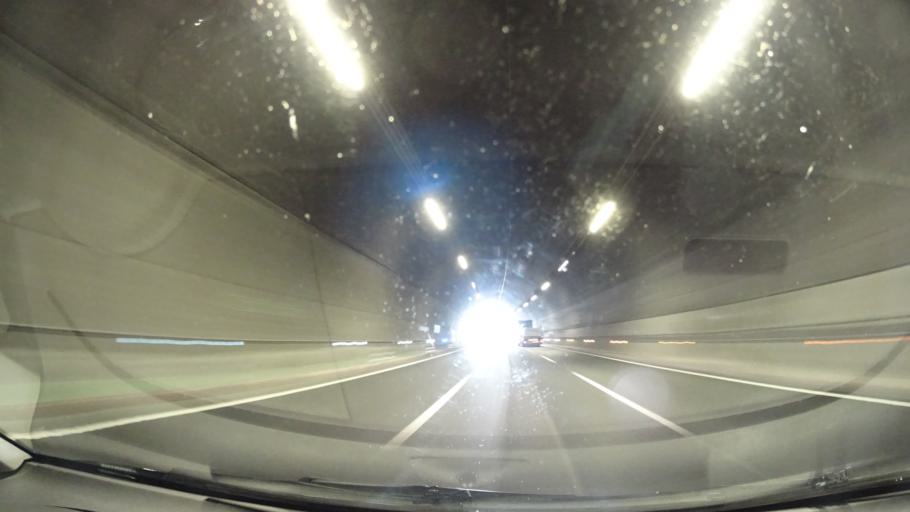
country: ES
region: Madrid
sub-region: Provincia de Madrid
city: Somosierra
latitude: 41.1357
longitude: -3.5825
